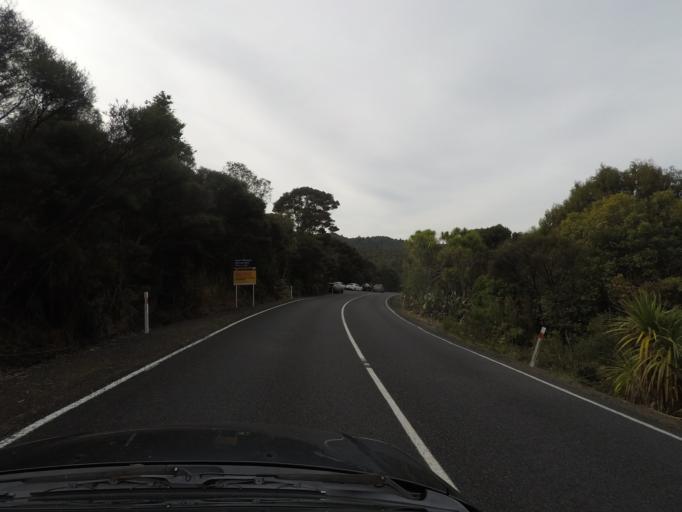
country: NZ
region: Auckland
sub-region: Auckland
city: Titirangi
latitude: -36.9371
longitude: 174.5560
